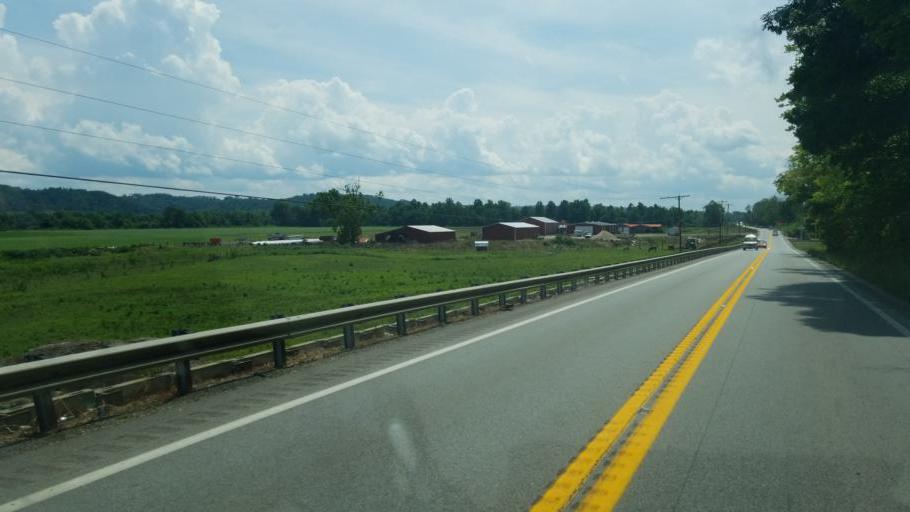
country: US
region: West Virginia
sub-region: Putnam County
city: Buffalo
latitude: 38.6426
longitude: -81.9745
